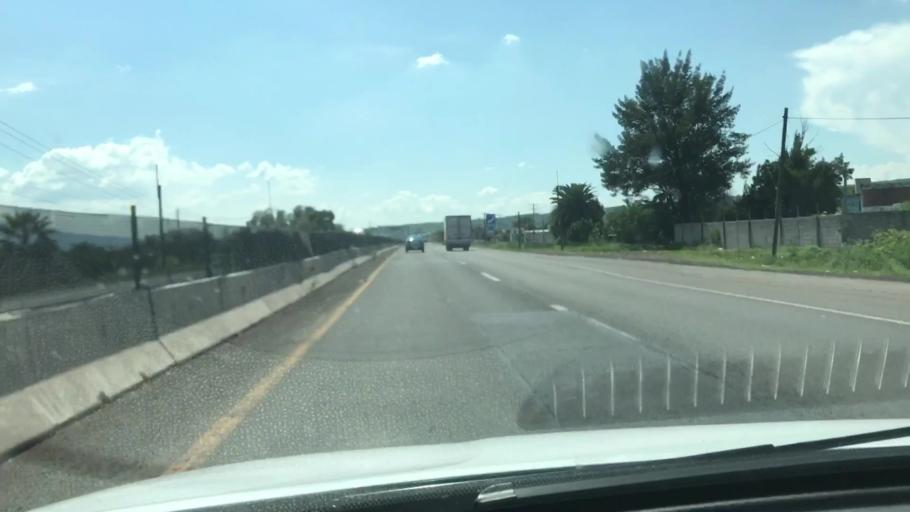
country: MX
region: Guanajuato
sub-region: Penjamo
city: Estacion la Piedad
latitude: 20.3887
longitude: -101.9404
